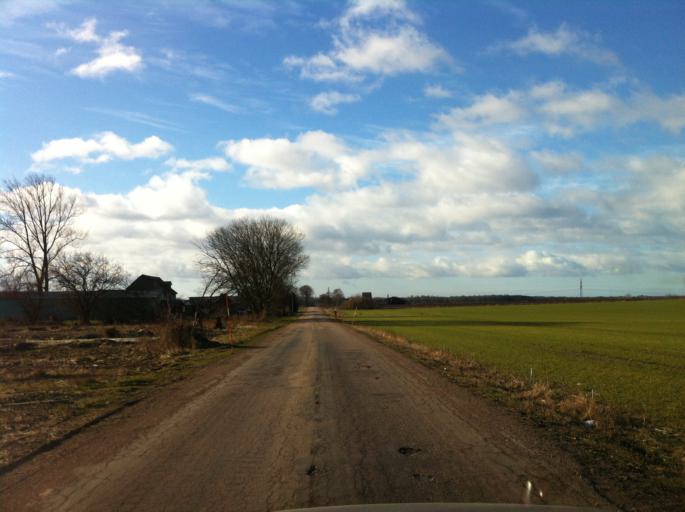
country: SE
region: Skane
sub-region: Landskrona
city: Asmundtorp
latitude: 55.9425
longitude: 12.9534
